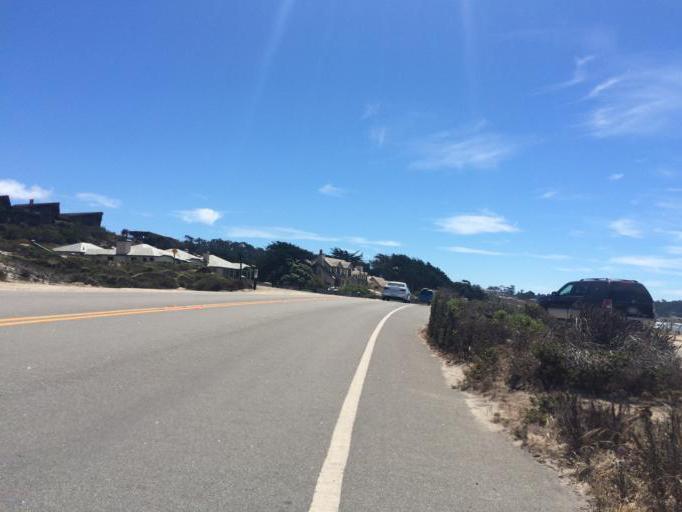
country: US
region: California
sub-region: Monterey County
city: Del Monte Forest
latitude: 36.5895
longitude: -121.9630
